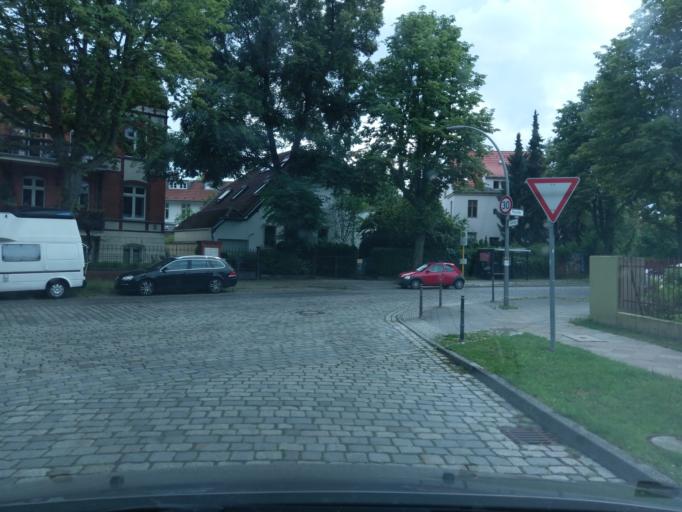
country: DE
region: Berlin
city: Lichterfelde
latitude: 52.4354
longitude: 13.2892
